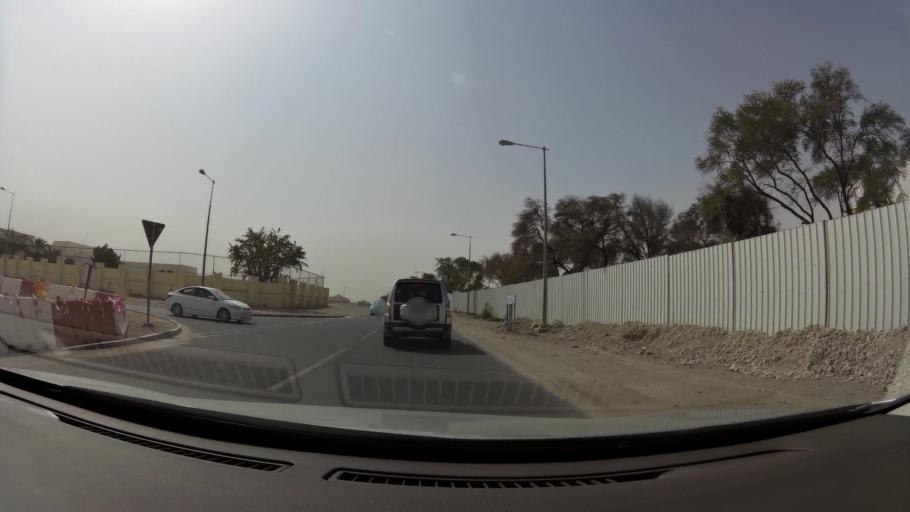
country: QA
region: Baladiyat ad Dawhah
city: Doha
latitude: 25.3029
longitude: 51.4769
